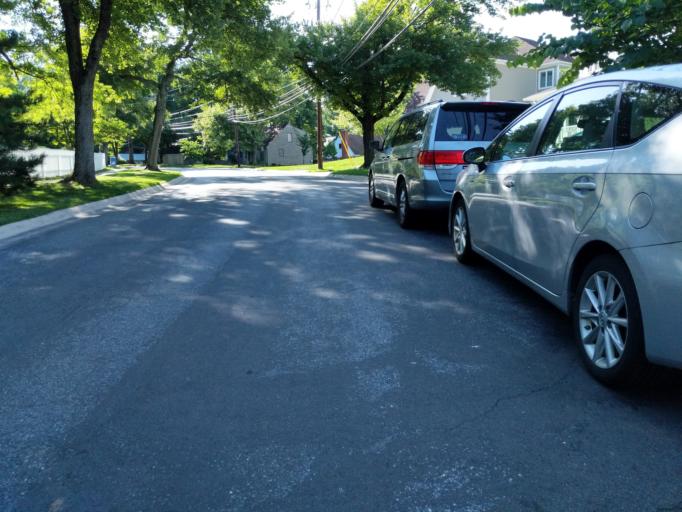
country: US
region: Maryland
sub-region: Montgomery County
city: North Bethesda
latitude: 39.0082
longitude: -77.1252
